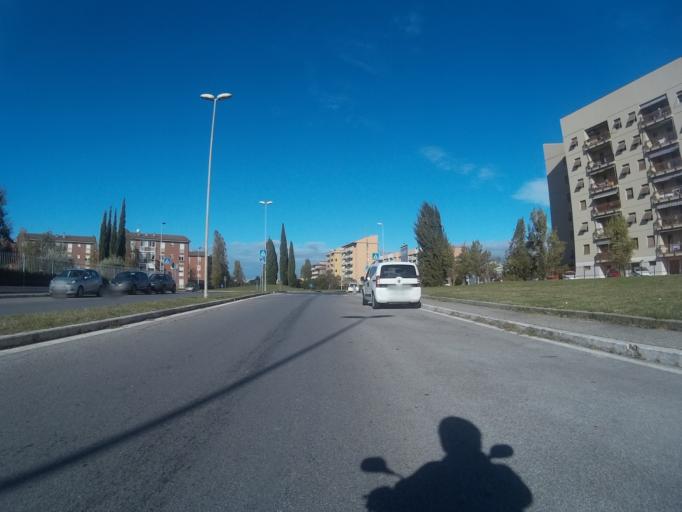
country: IT
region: Tuscany
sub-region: Provincia di Livorno
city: Livorno
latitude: 43.5259
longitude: 10.3453
